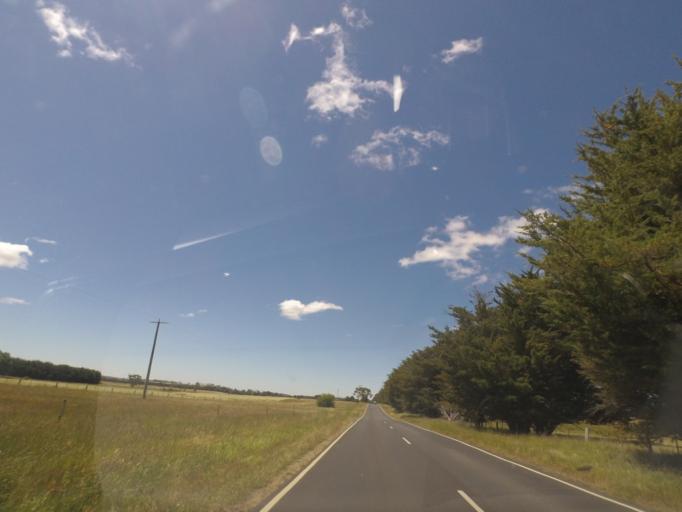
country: AU
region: Victoria
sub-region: Mount Alexander
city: Castlemaine
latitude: -37.2488
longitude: 144.3211
